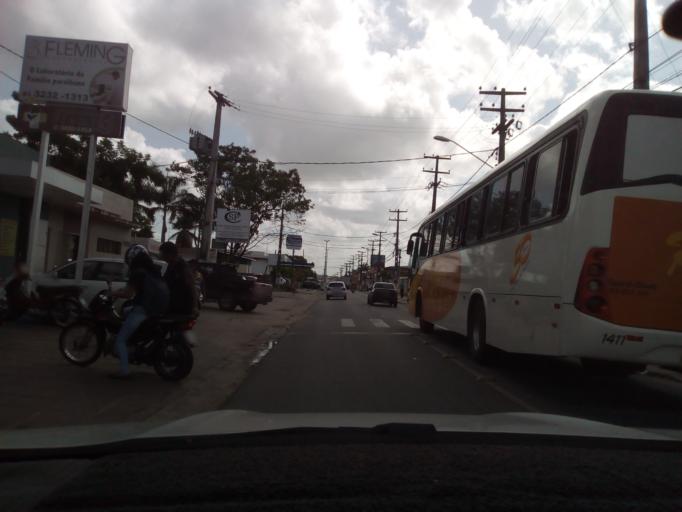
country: BR
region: Paraiba
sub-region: Bayeux
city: Bayeux
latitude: -7.1247
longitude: -34.9238
